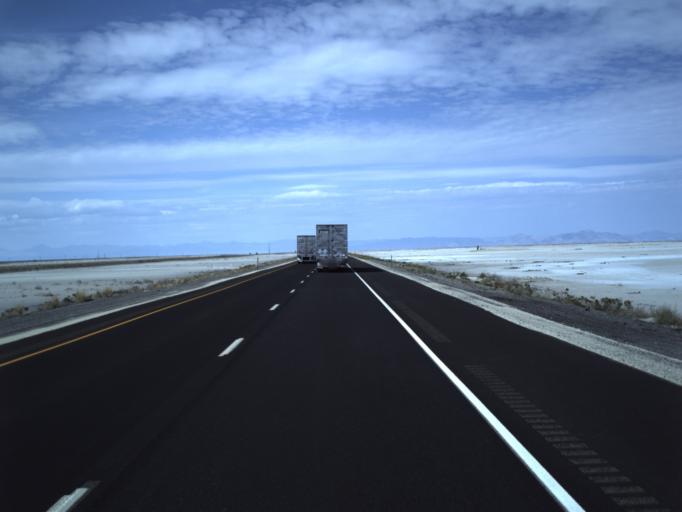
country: US
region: Utah
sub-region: Tooele County
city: Wendover
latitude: 40.7313
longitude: -113.4759
